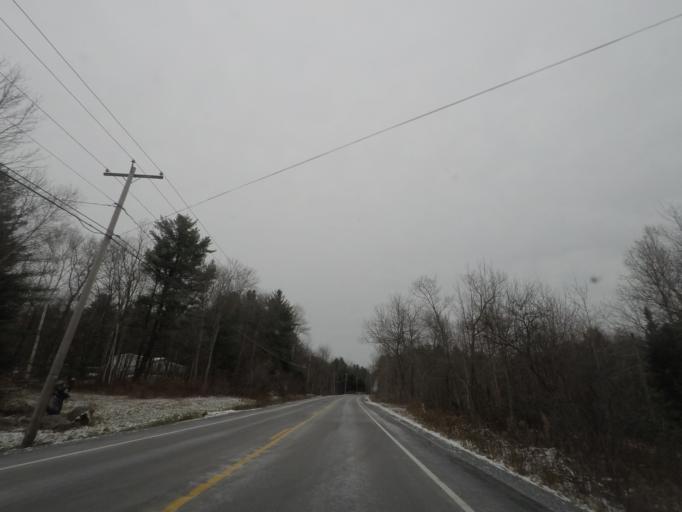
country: US
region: New York
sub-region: Rensselaer County
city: Hoosick Falls
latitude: 42.7698
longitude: -73.4236
